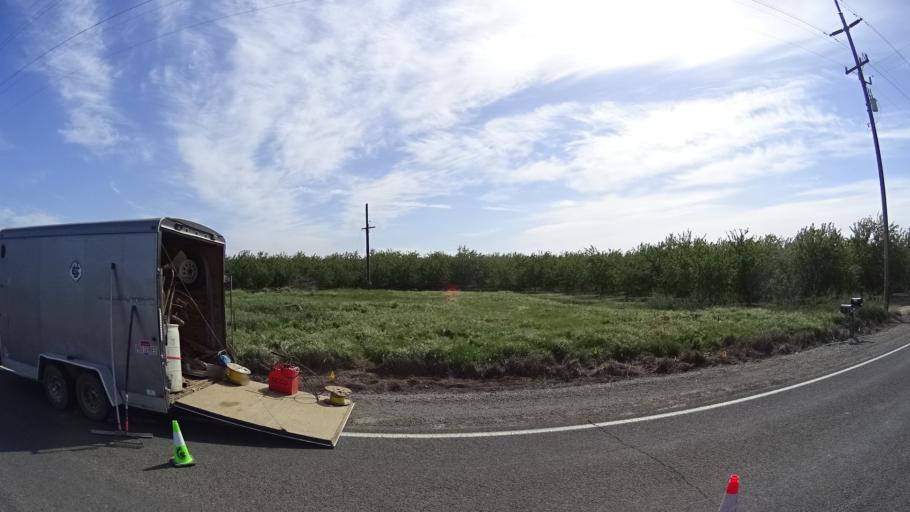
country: US
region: California
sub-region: Glenn County
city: Hamilton City
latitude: 39.6485
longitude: -122.0078
